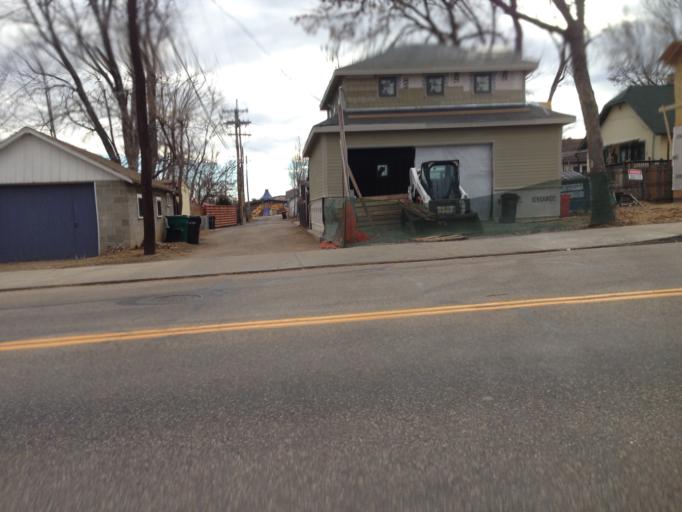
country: US
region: Colorado
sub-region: Boulder County
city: Louisville
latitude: 39.9770
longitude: -105.1386
